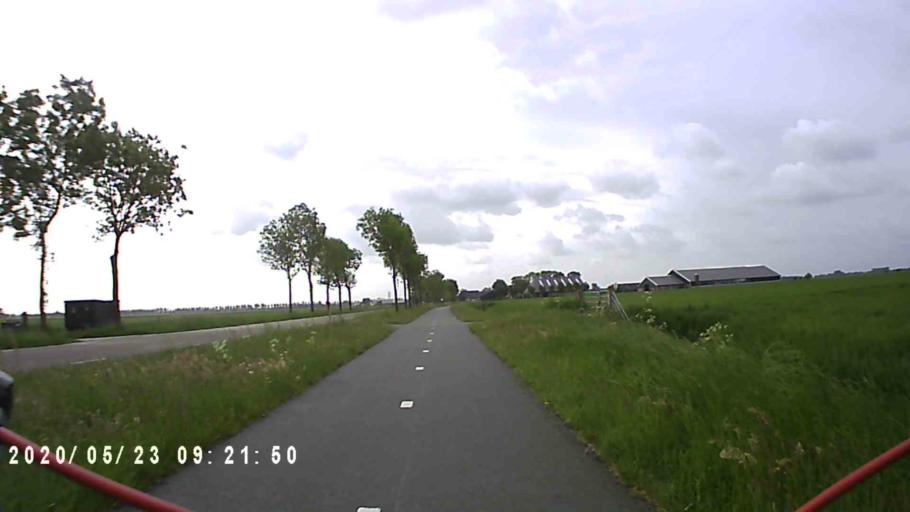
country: NL
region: Groningen
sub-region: Gemeente Bedum
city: Bedum
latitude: 53.2917
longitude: 6.6782
